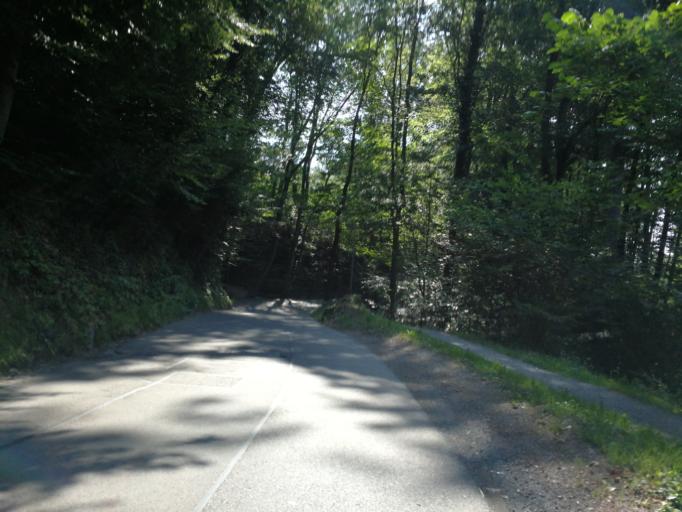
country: CH
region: Zurich
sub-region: Bezirk Meilen
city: Erlenbach / rechts des Dorfbachs oberhalb Bahnlinie
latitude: 47.3038
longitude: 8.6080
